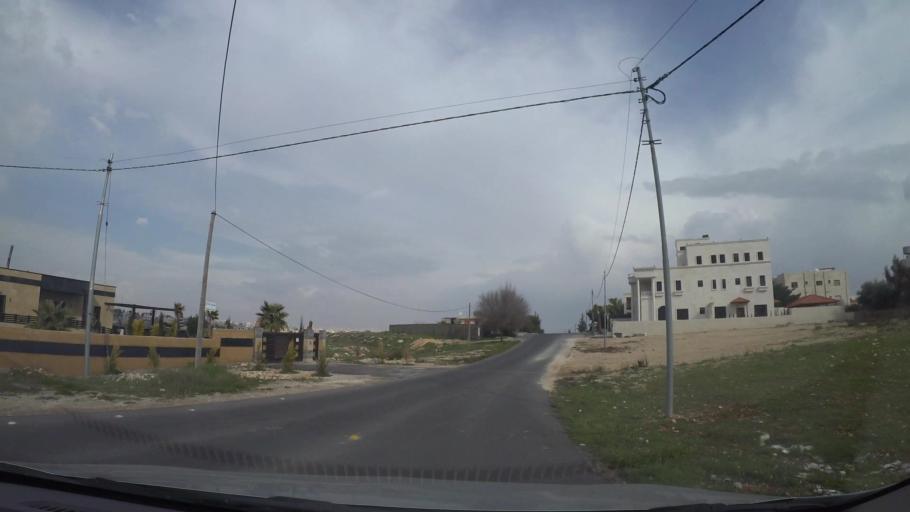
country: JO
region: Amman
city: Umm as Summaq
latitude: 31.8879
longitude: 35.8677
